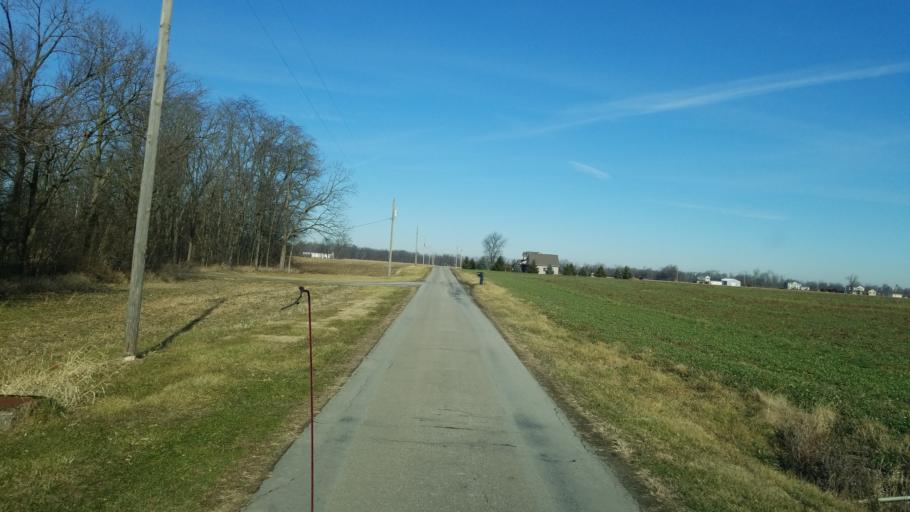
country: US
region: Ohio
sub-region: Putnam County
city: Pandora
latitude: 41.0017
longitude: -83.9377
